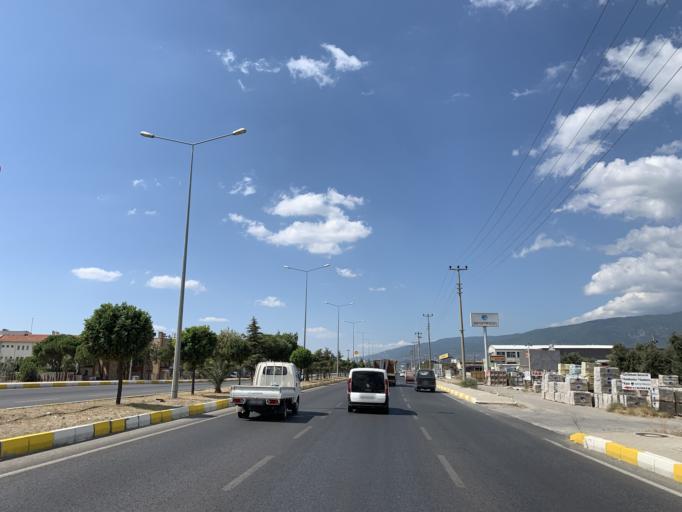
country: TR
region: Balikesir
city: Edremit
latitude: 39.5965
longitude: 26.9665
